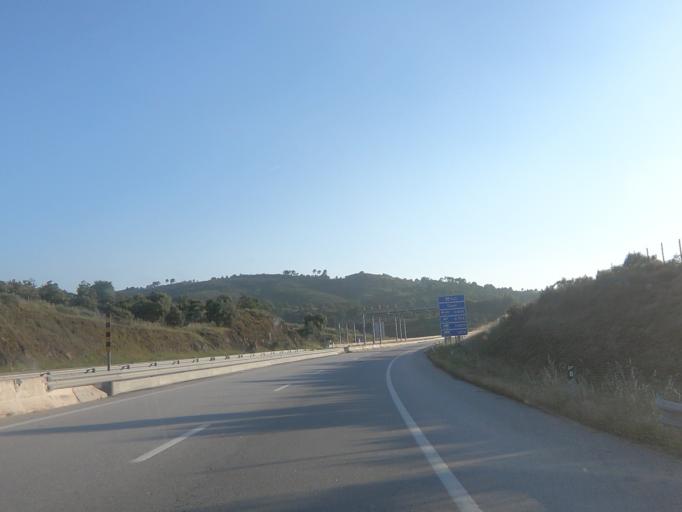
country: PT
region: Guarda
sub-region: Celorico da Beira
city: Celorico da Beira
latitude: 40.6269
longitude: -7.3614
